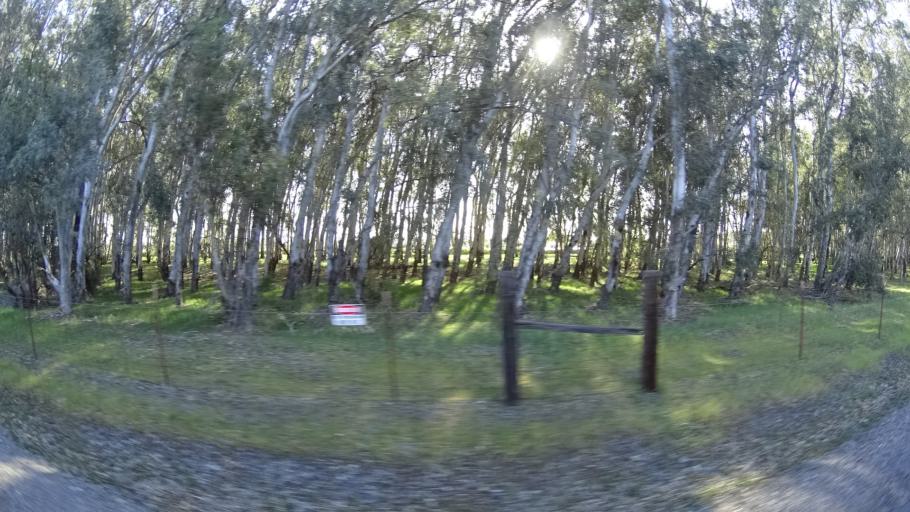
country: US
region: California
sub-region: Glenn County
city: Orland
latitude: 39.7675
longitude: -122.2154
